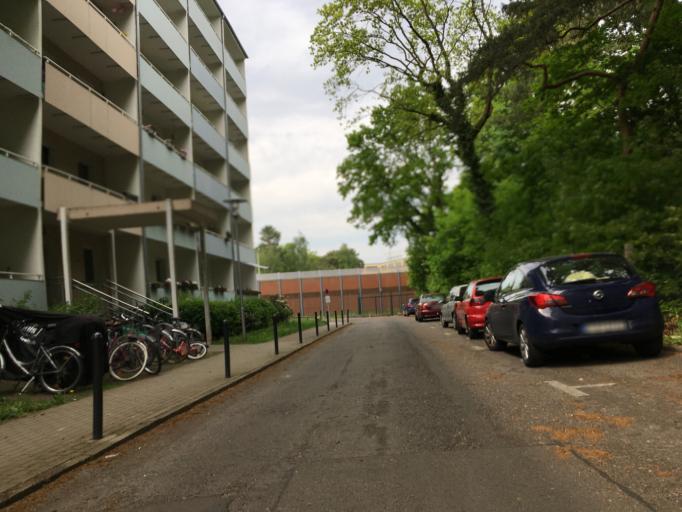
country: DE
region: Berlin
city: Buch
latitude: 52.6278
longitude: 13.5107
